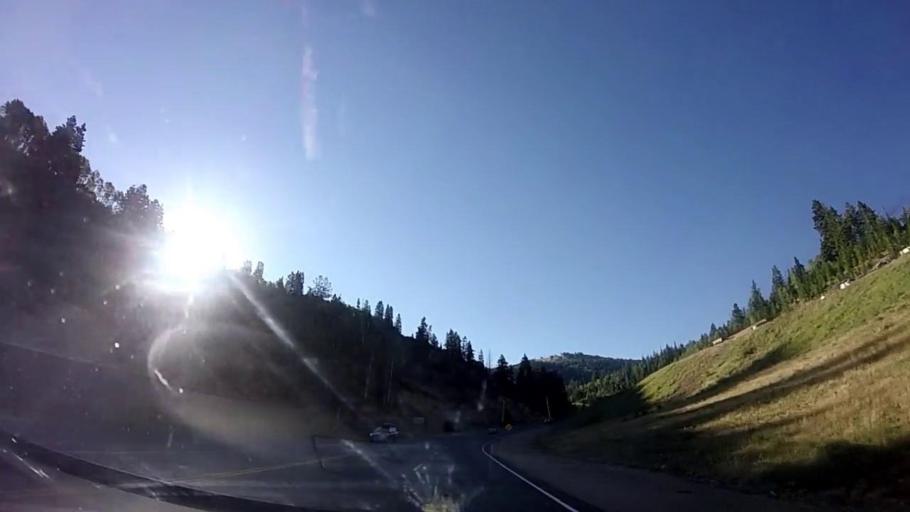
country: US
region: Utah
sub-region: Summit County
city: Park City
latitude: 40.6236
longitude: -111.4954
